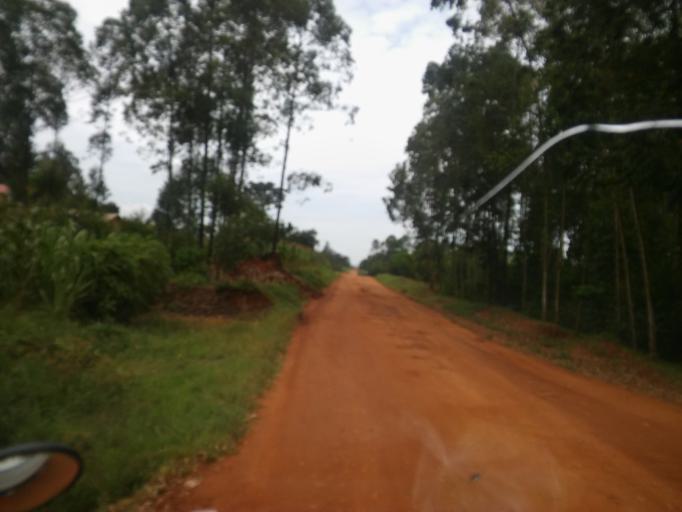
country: UG
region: Eastern Region
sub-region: Mbale District
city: Mbale
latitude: 0.9743
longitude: 34.2060
